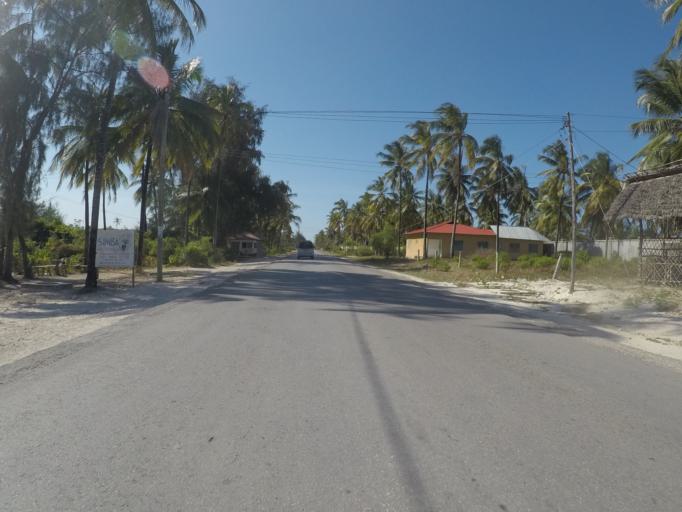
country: TZ
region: Zanzibar Central/South
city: Nganane
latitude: -6.2592
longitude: 39.5326
